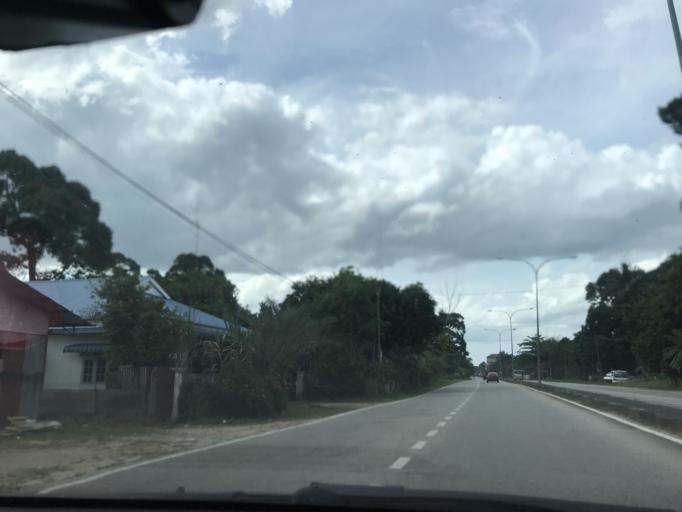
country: MY
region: Kelantan
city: Kampong Pangkal Kalong
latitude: 5.9195
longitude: 102.1888
